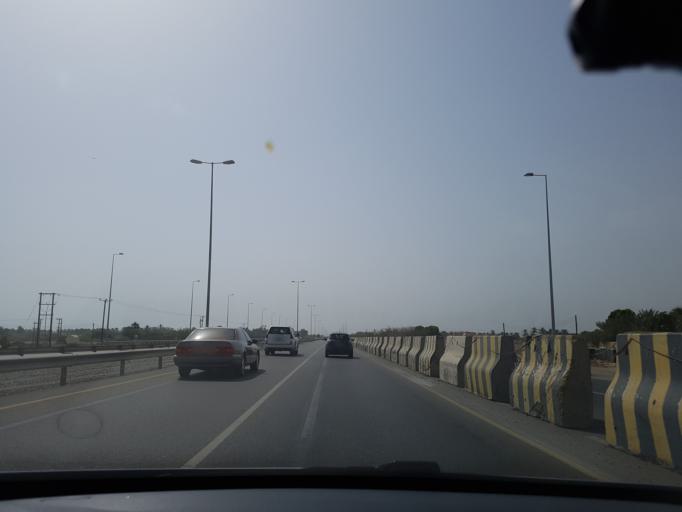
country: OM
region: Al Batinah
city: Al Khaburah
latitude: 23.9980
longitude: 57.0619
